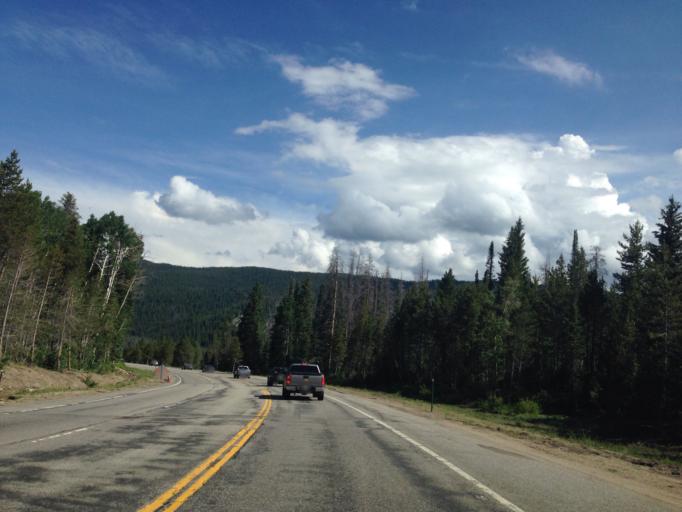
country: US
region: Colorado
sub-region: Routt County
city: Steamboat Springs
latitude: 40.3556
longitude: -106.7500
